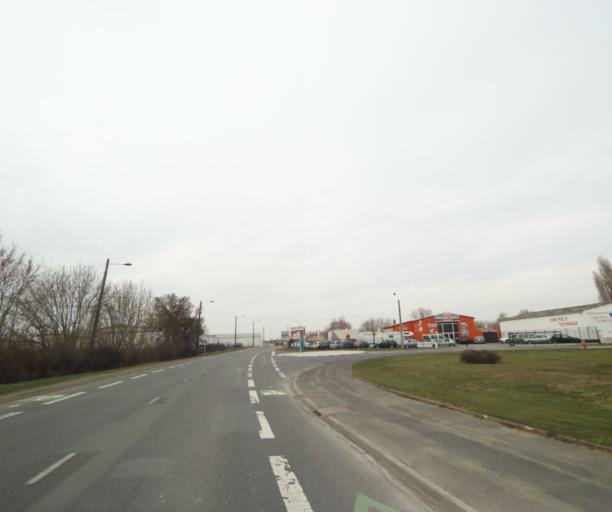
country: FR
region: Poitou-Charentes
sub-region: Departement des Deux-Sevres
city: Bessines
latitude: 46.3122
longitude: -0.4962
